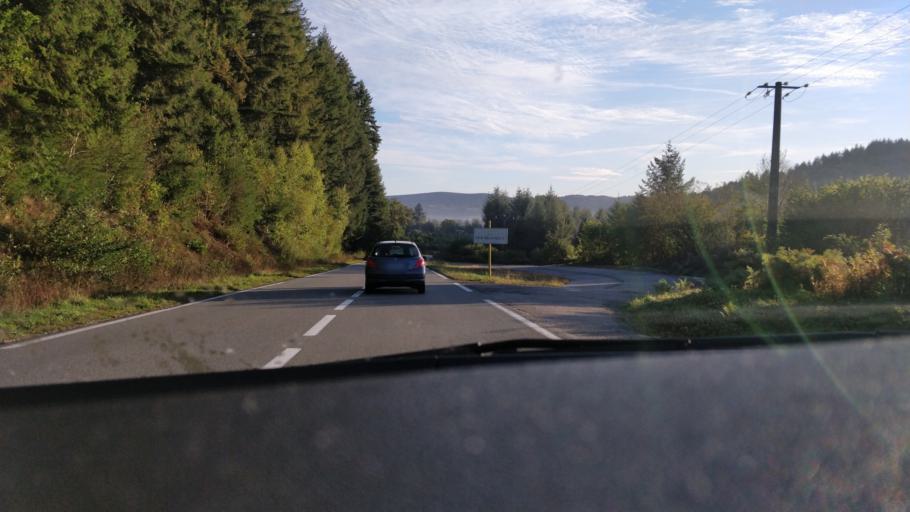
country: FR
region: Limousin
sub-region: Departement de la Creuse
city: Bourganeuf
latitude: 45.9503
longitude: 1.7195
